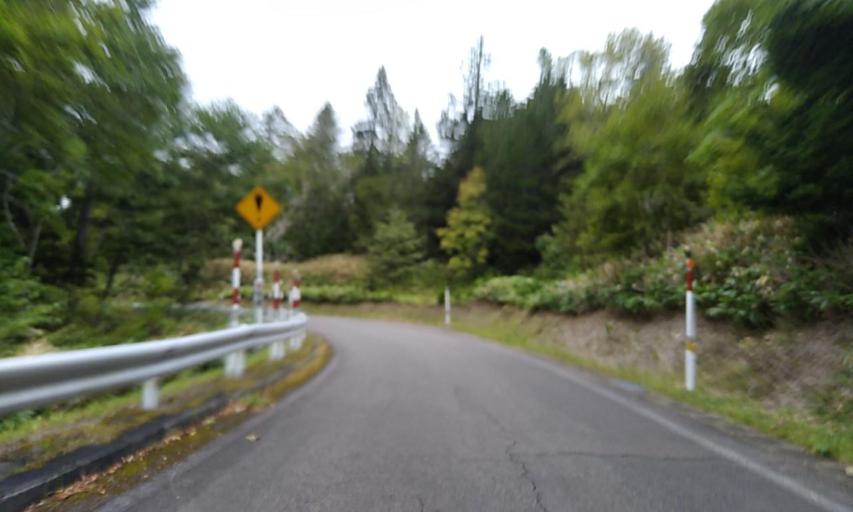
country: JP
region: Hokkaido
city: Bihoro
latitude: 43.5674
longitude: 144.2060
